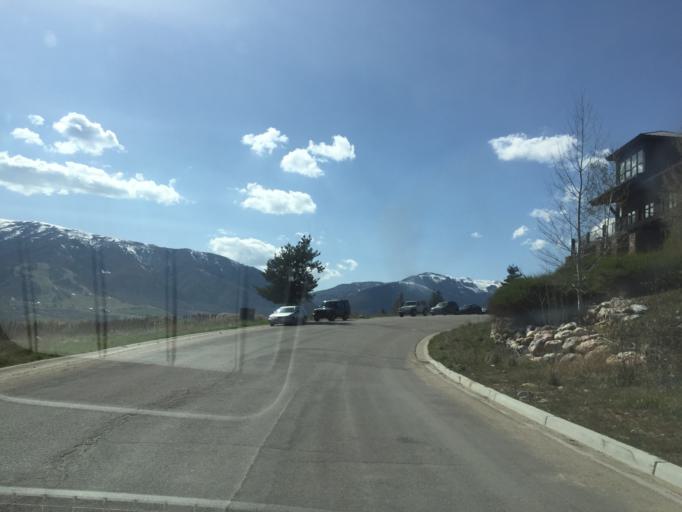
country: US
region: Utah
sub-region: Weber County
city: Wolf Creek
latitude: 41.3241
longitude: -111.8271
